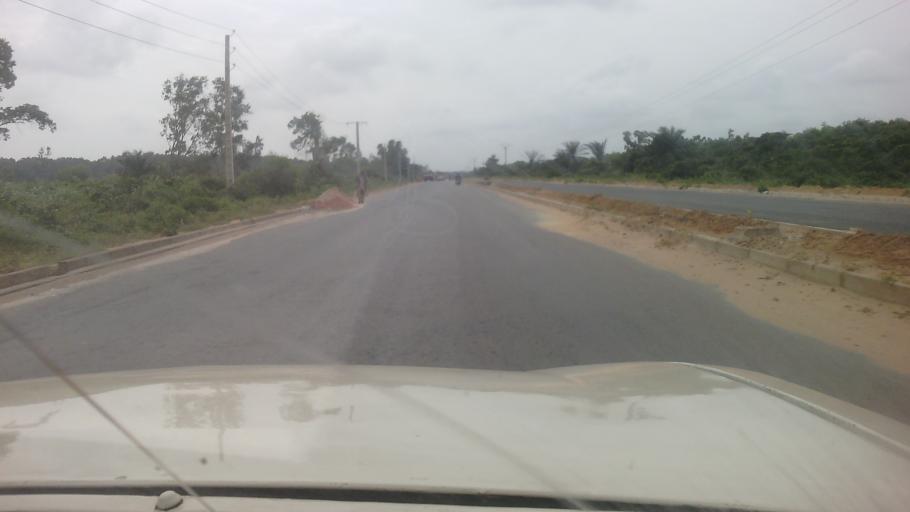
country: BJ
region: Atlantique
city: Ouidah
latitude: 6.3768
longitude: 2.1557
